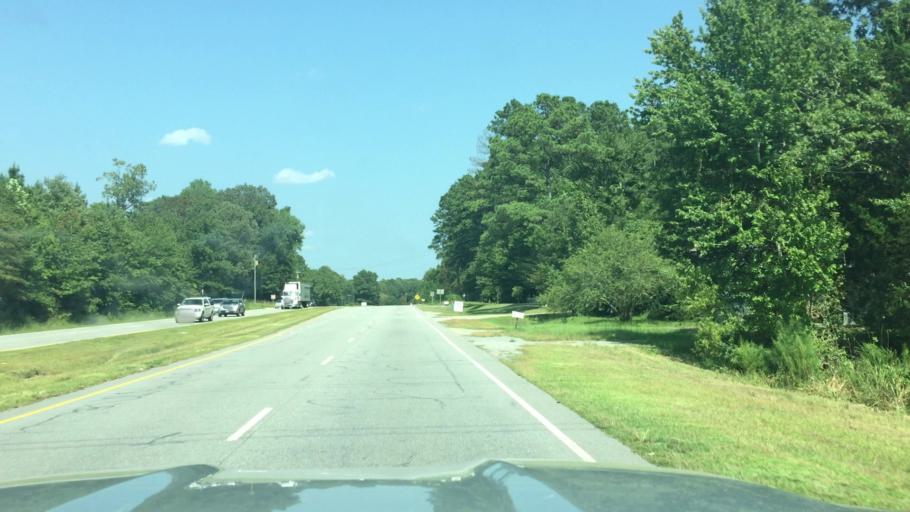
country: US
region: North Carolina
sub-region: Martin County
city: Williamston
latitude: 35.8089
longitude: -76.9371
